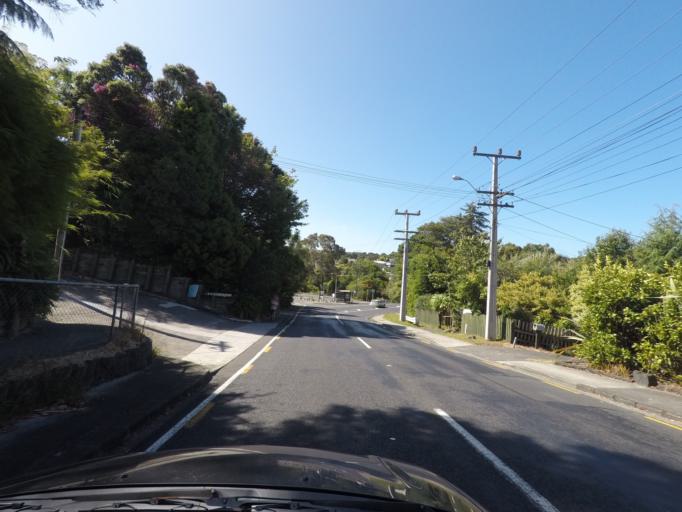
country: NZ
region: Auckland
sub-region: Auckland
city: Waitakere
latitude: -36.9249
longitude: 174.6555
